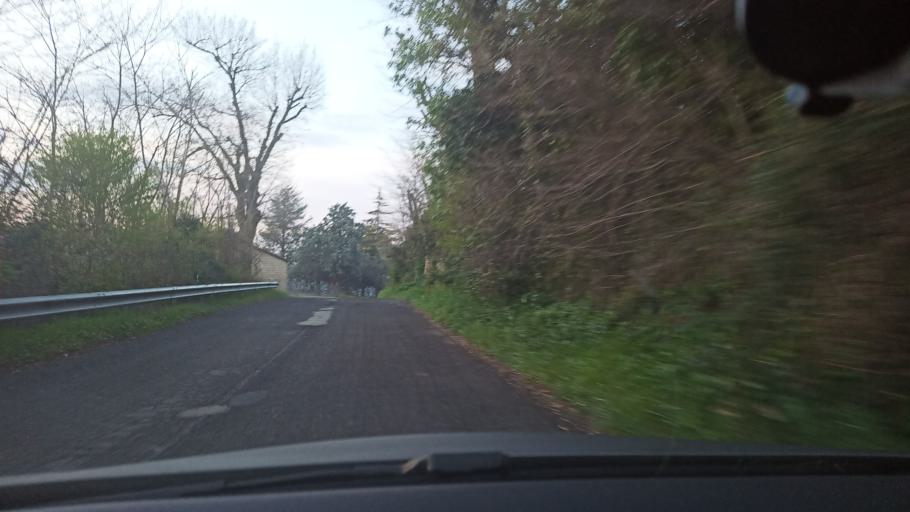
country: IT
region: Latium
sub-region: Provincia di Rieti
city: Torri in Sabina
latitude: 42.3513
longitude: 12.6498
